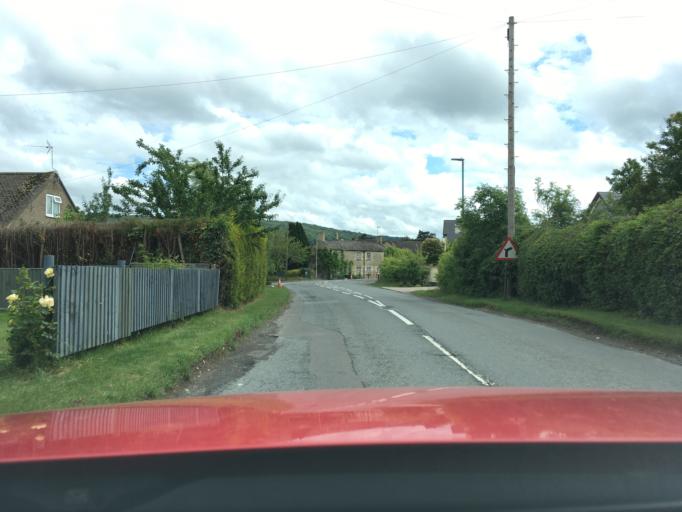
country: GB
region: England
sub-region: Gloucestershire
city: Winchcombe
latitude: 51.9682
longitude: -1.9654
